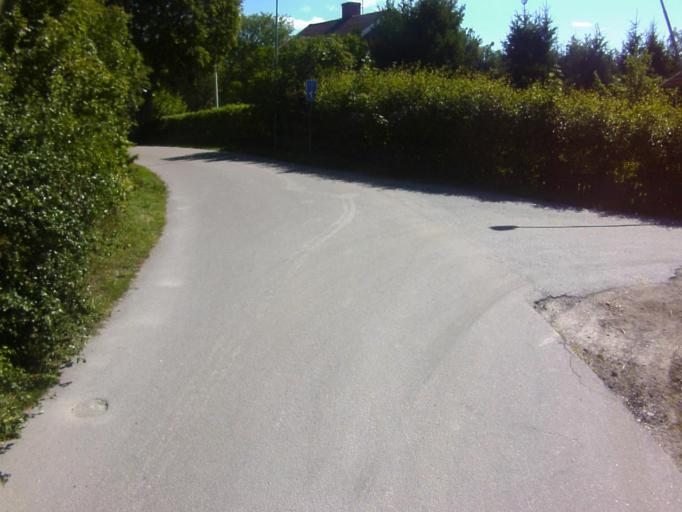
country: SE
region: Soedermanland
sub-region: Eskilstuna Kommun
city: Hallbybrunn
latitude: 59.3738
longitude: 16.4577
